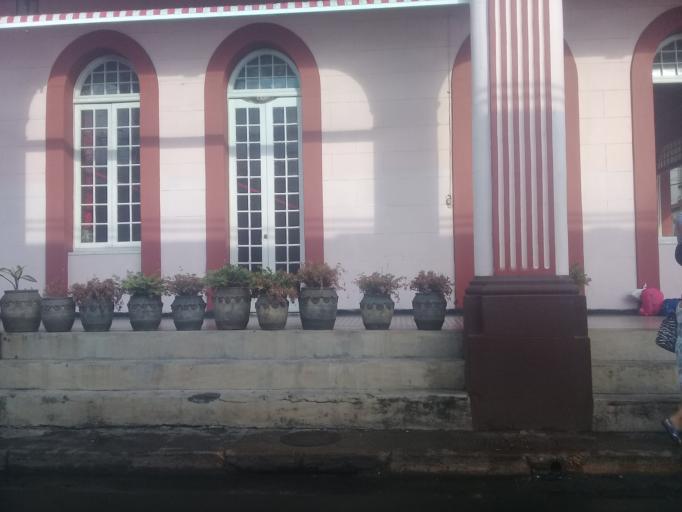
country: CU
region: Pinar del Rio
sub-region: Municipio de Pinar del Rio
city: Pinar del Rio
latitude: 22.4162
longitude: -83.6984
